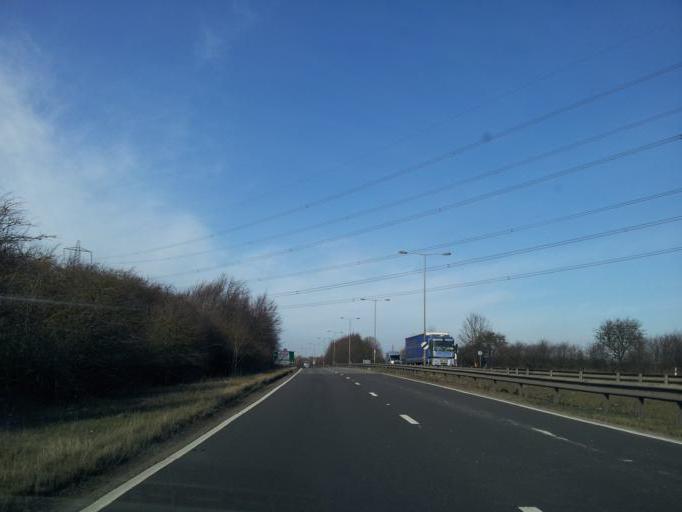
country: GB
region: England
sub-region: Lincolnshire
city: Grantham
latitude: 52.8703
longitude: -0.6302
